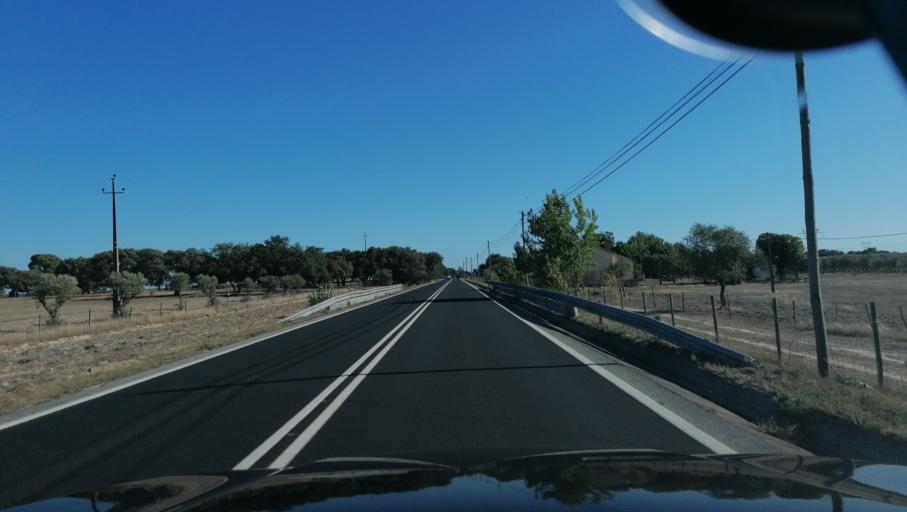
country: PT
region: Santarem
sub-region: Benavente
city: Poceirao
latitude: 38.8194
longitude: -8.8809
